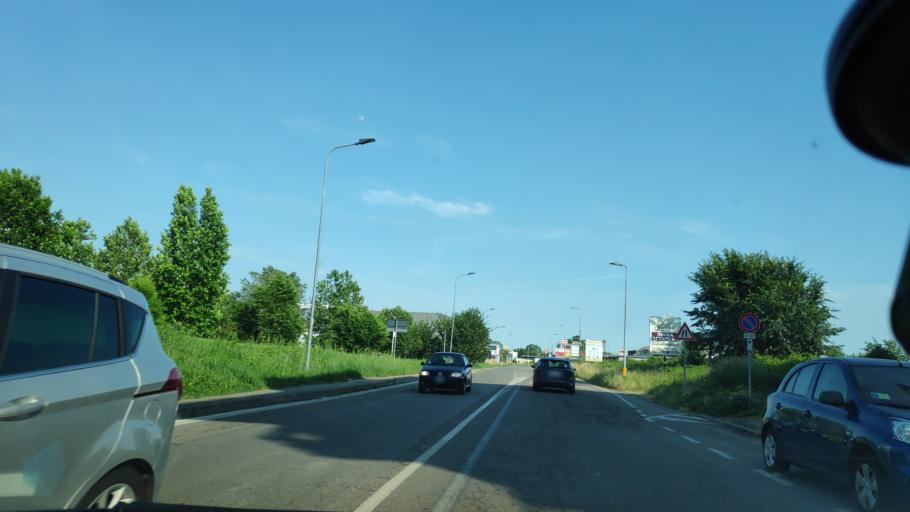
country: IT
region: Lombardy
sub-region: Citta metropolitana di Milano
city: Fizzonasco
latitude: 45.3789
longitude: 9.1817
